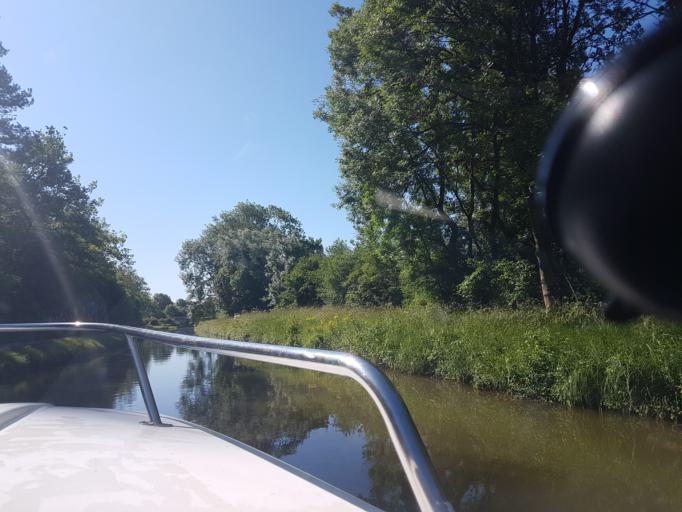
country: FR
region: Bourgogne
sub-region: Departement de la Nievre
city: Clamecy
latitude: 47.5339
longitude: 3.6002
